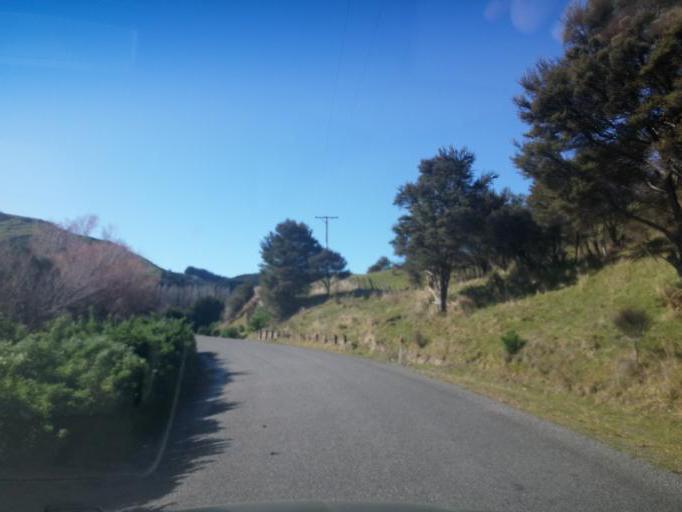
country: NZ
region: Wellington
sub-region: South Wairarapa District
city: Waipawa
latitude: -41.4215
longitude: 175.4972
